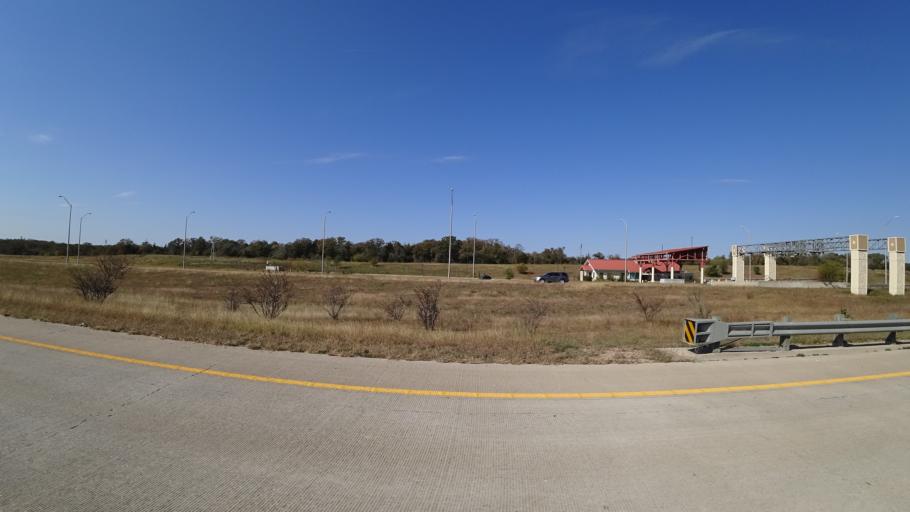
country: US
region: Texas
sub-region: Travis County
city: Hornsby Bend
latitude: 30.2688
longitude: -97.5945
